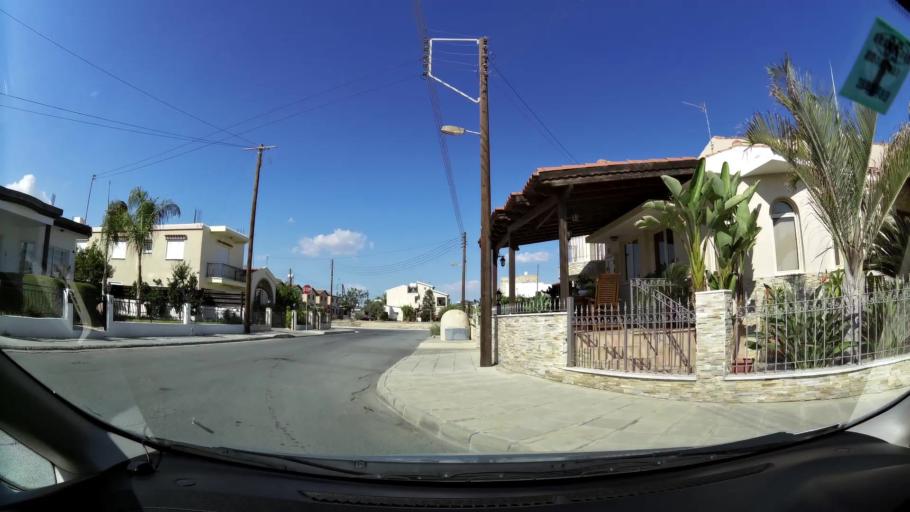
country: CY
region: Larnaka
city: Livadia
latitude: 34.9468
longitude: 33.6315
